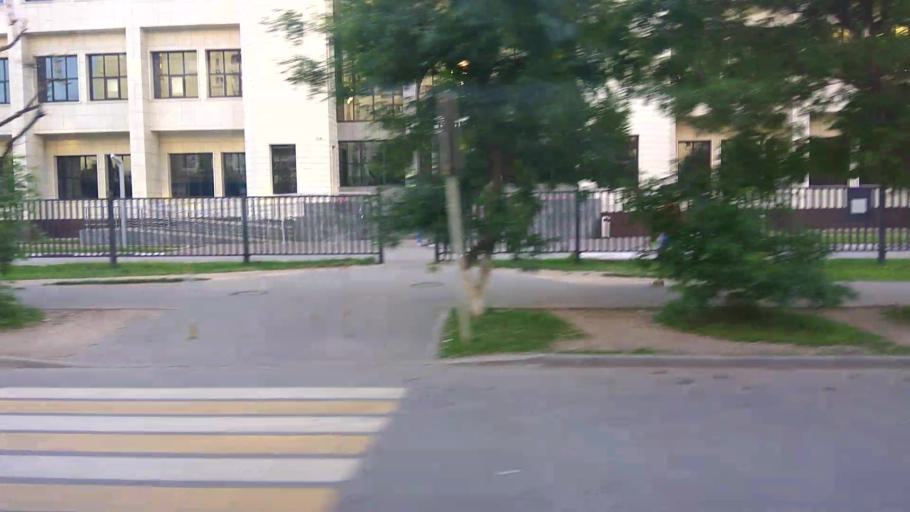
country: RU
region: Moskovskaya
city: Yubileyny
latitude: 55.9190
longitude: 37.8681
